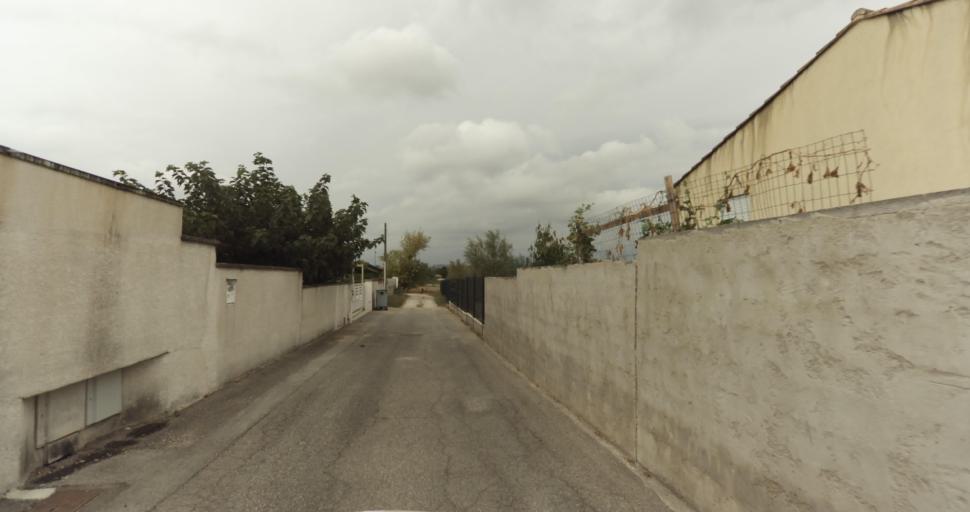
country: FR
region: Provence-Alpes-Cote d'Azur
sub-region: Departement des Bouches-du-Rhone
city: Saint-Victoret
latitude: 43.4124
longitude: 5.2592
